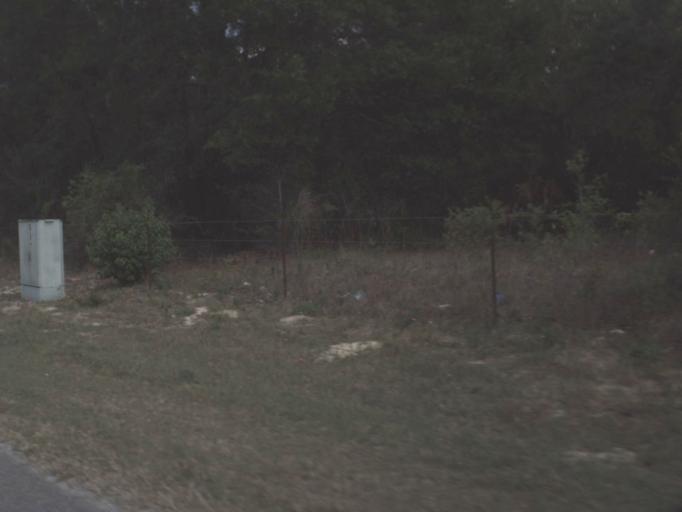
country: US
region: Florida
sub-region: Lake County
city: Mount Dora
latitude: 28.8006
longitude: -81.6010
